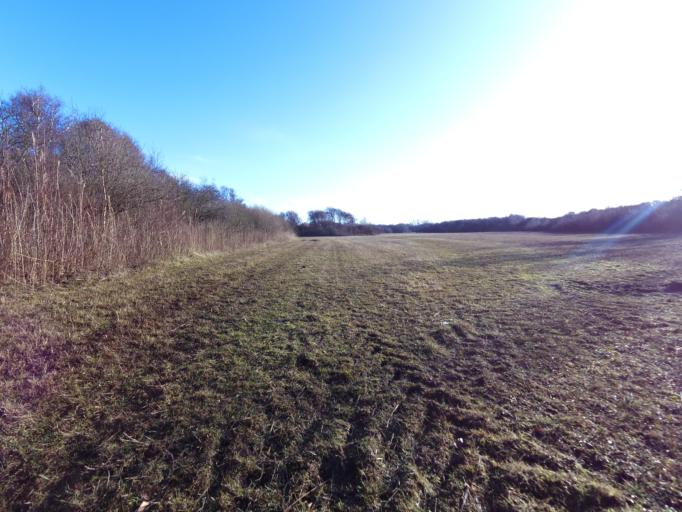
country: NL
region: South Holland
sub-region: Gemeente Rotterdam
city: Hoek van Holland
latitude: 51.9185
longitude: 4.0582
